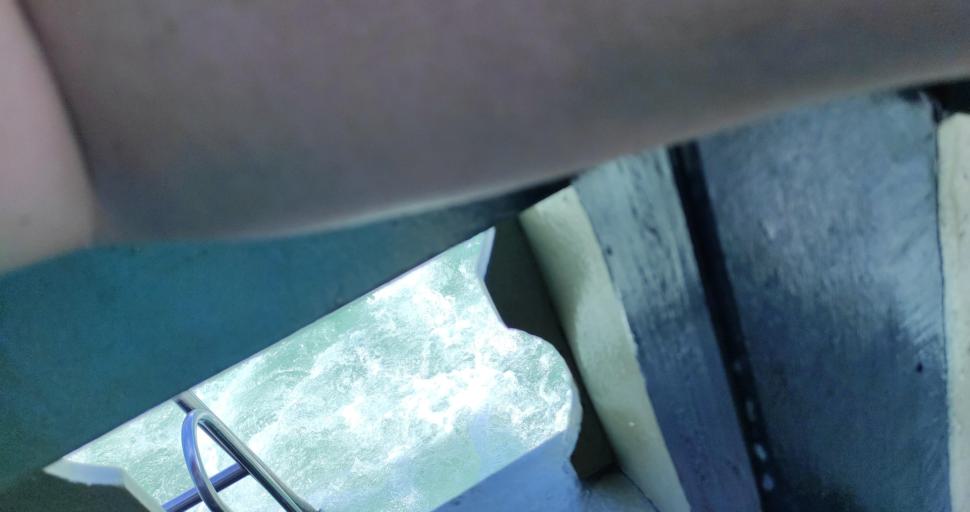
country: BR
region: Santa Catarina
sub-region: Porto Belo
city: Porto Belo
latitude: -27.2213
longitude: -48.5086
